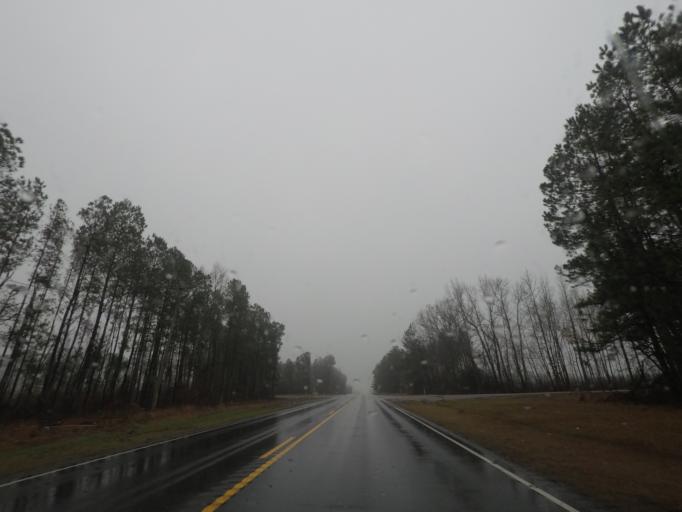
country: US
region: North Carolina
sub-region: Scotland County
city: Laurinburg
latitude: 34.8243
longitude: -79.4590
